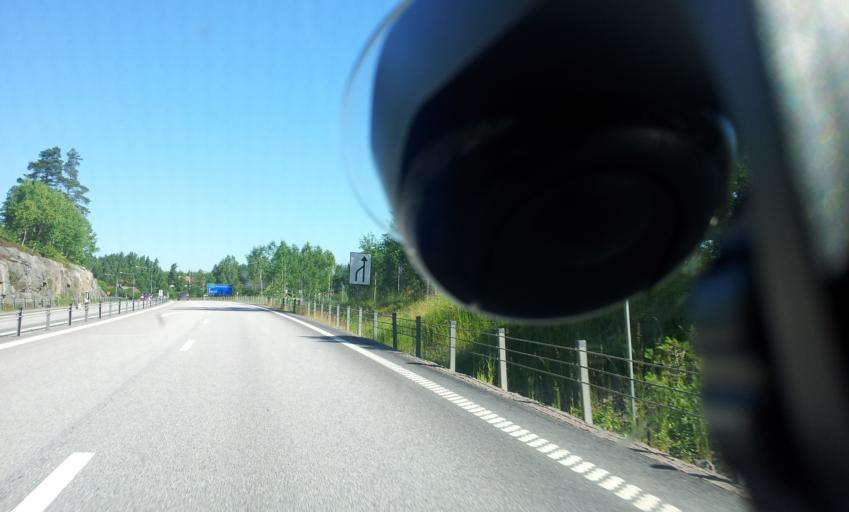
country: SE
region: OEstergoetland
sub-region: Soderkopings Kommun
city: Soederkoeping
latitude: 58.3935
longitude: 16.4108
